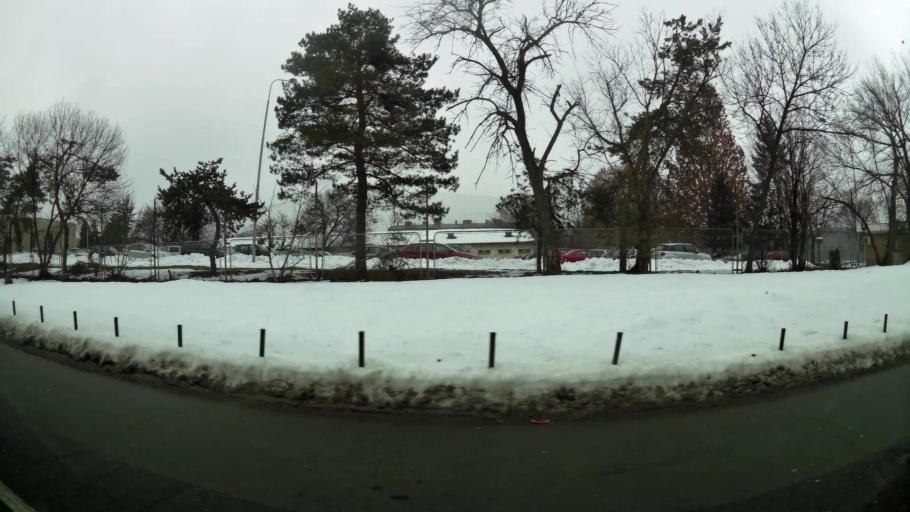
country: RS
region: Central Serbia
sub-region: Belgrade
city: Savski Venac
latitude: 44.7677
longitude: 20.4617
